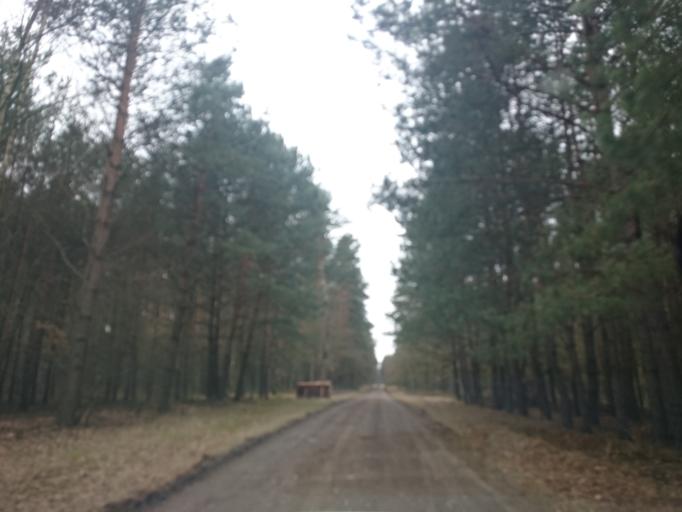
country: PL
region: Kujawsko-Pomorskie
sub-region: Powiat golubsko-dobrzynski
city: Ciechocin
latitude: 53.0761
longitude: 18.9216
